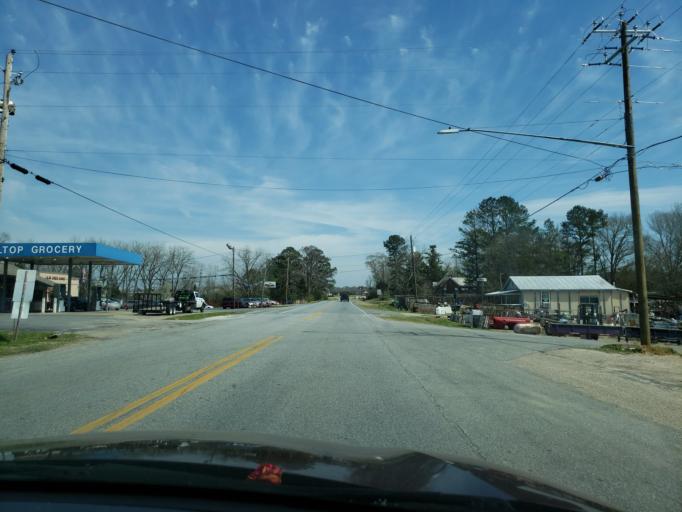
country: US
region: Alabama
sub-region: Elmore County
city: Tallassee
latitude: 32.5515
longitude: -85.8413
